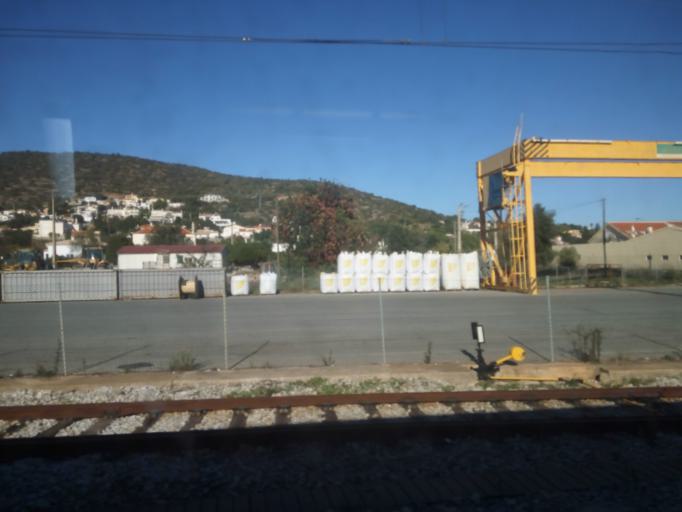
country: PT
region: Faro
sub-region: Loule
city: Almancil
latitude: 37.1047
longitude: -8.0601
